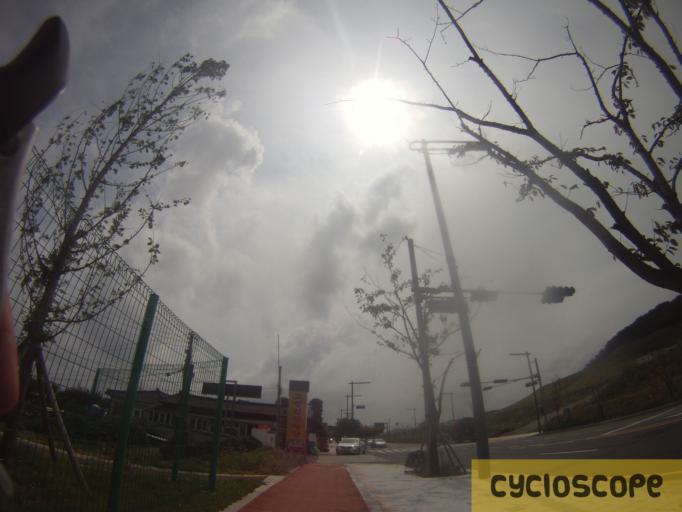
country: KR
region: Busan
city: Kijang
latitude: 35.1952
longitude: 129.2215
